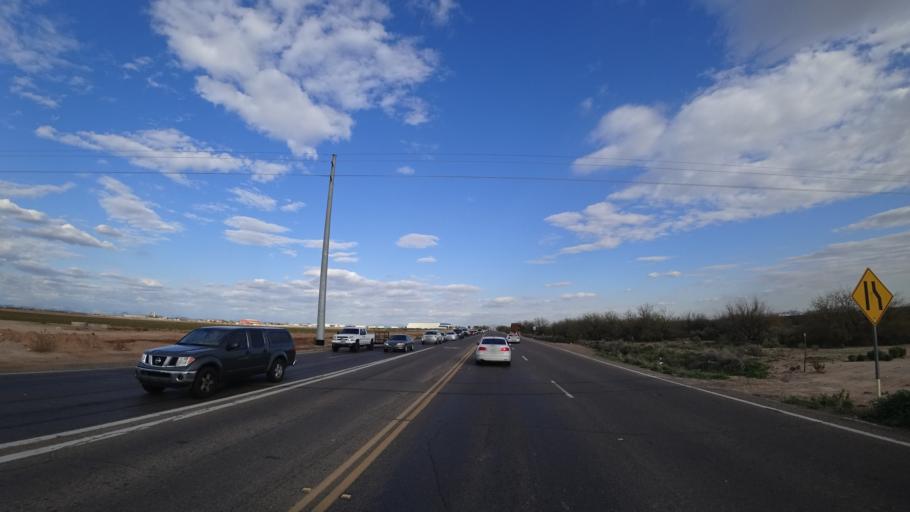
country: US
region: Arizona
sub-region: Maricopa County
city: Youngtown
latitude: 33.5511
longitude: -112.3411
